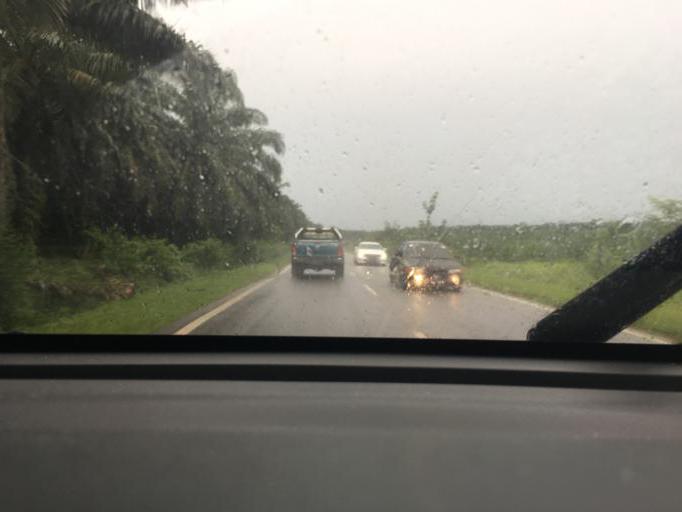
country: MY
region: Kedah
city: Bedong
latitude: 5.6577
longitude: 100.6317
